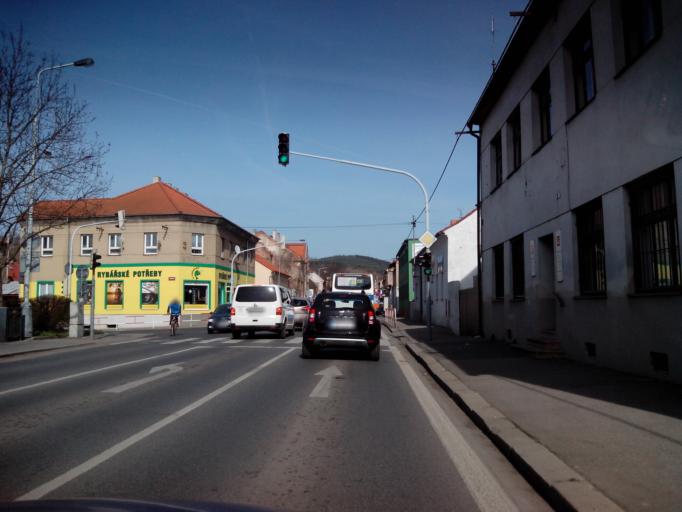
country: CZ
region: Central Bohemia
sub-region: Okres Beroun
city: Beroun
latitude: 49.9680
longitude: 14.0779
